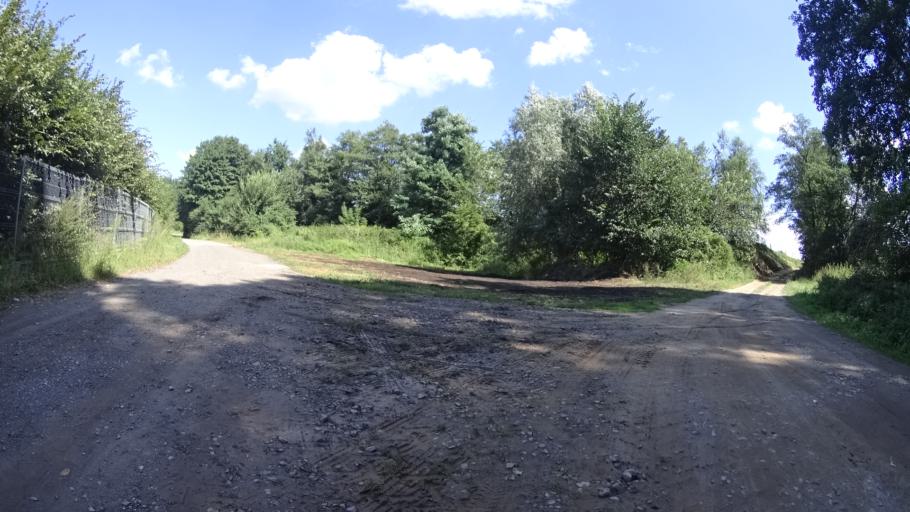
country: PL
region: Masovian Voivodeship
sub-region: Powiat grojecki
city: Mogielnica
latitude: 51.6703
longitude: 20.7450
